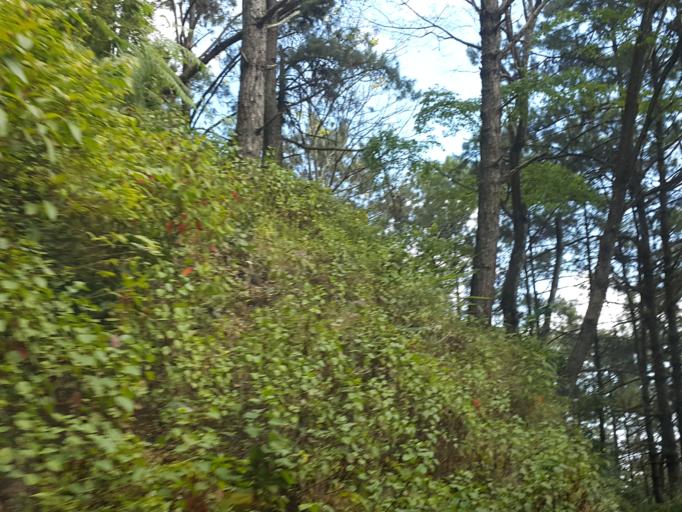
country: TH
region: Chiang Mai
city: Wiang Haeng
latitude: 19.5539
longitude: 98.8136
